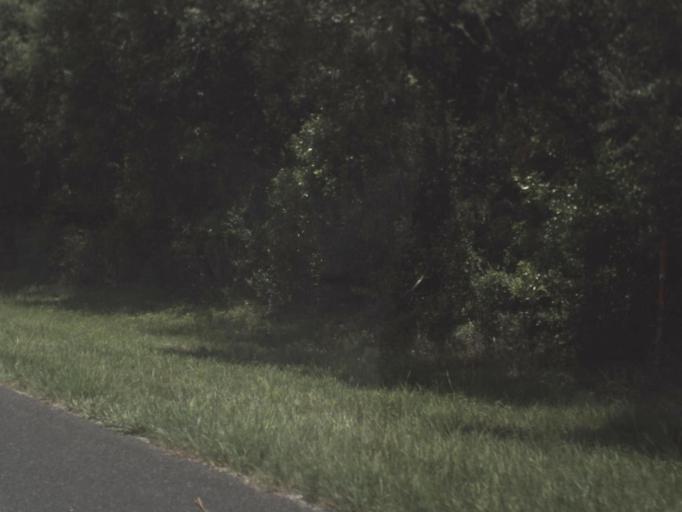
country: US
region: Florida
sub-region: Levy County
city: Manatee Road
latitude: 29.5674
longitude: -82.9107
